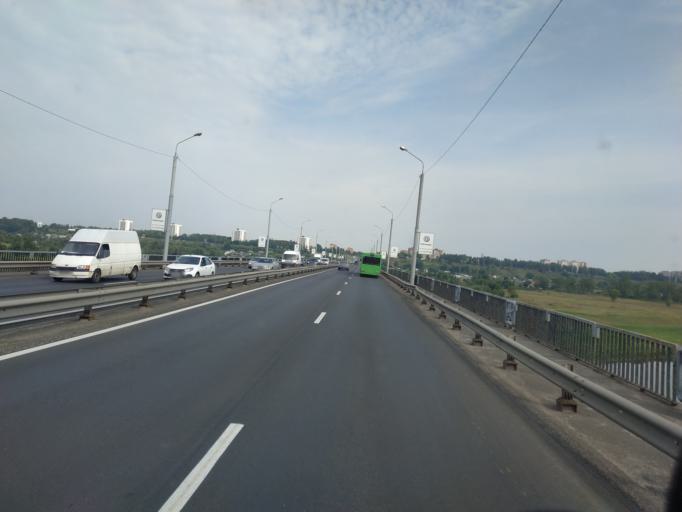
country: BY
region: Mogilev
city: Mahilyow
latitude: 53.8906
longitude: 30.3757
